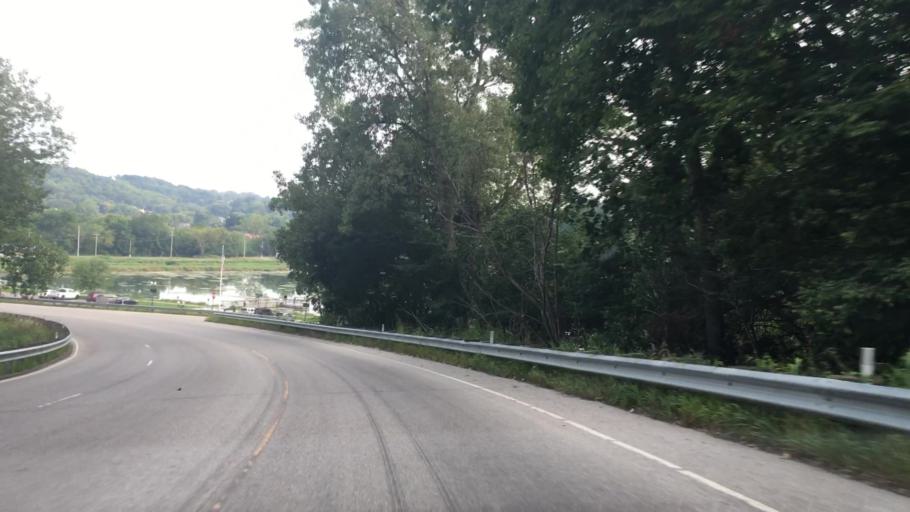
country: US
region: Minnesota
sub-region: Fillmore County
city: Preston
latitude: 43.7215
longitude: -91.9809
